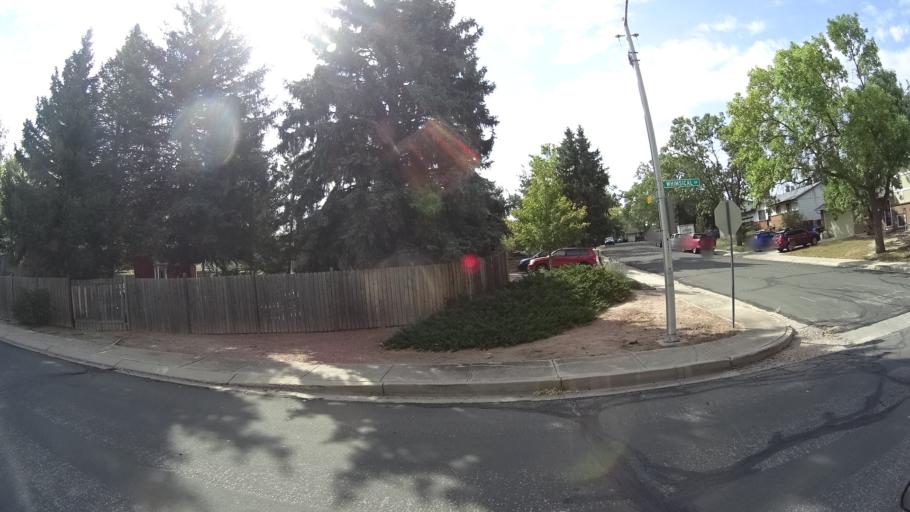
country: US
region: Colorado
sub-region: El Paso County
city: Cimarron Hills
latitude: 38.8793
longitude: -104.7389
